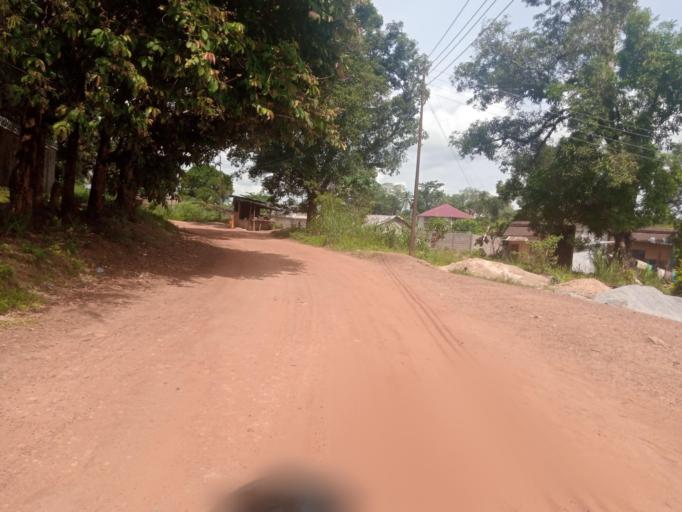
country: SL
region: Southern Province
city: Bo
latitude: 7.9687
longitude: -11.7548
